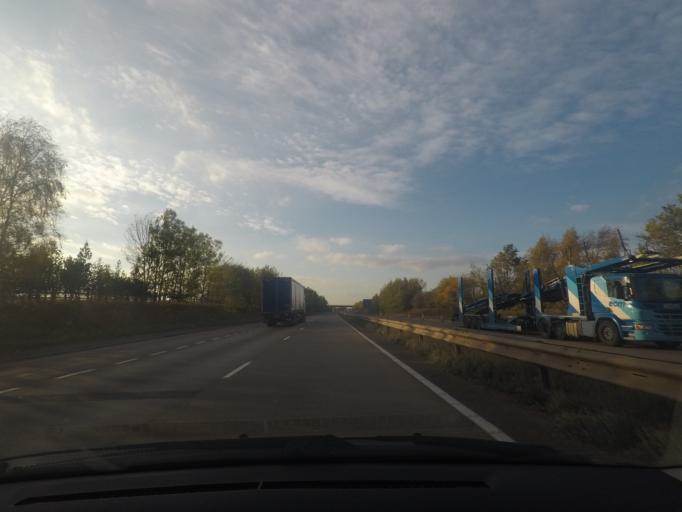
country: GB
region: England
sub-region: North East Lincolnshire
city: Immingham
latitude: 53.6012
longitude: -0.2133
